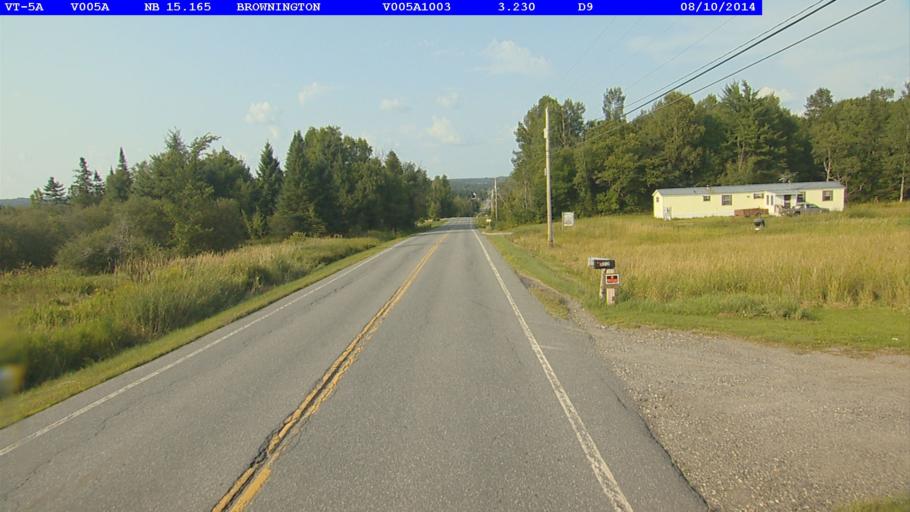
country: US
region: Vermont
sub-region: Orleans County
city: Newport
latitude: 44.8283
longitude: -72.0692
